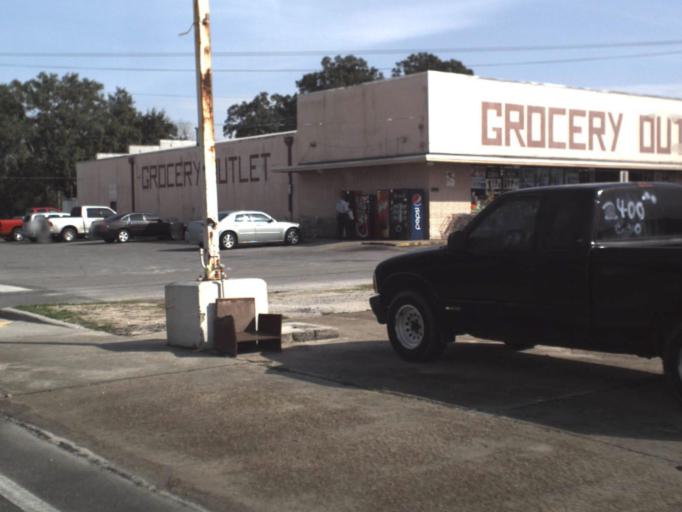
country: US
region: Florida
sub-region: Bay County
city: Panama City
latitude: 30.1588
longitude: -85.6584
